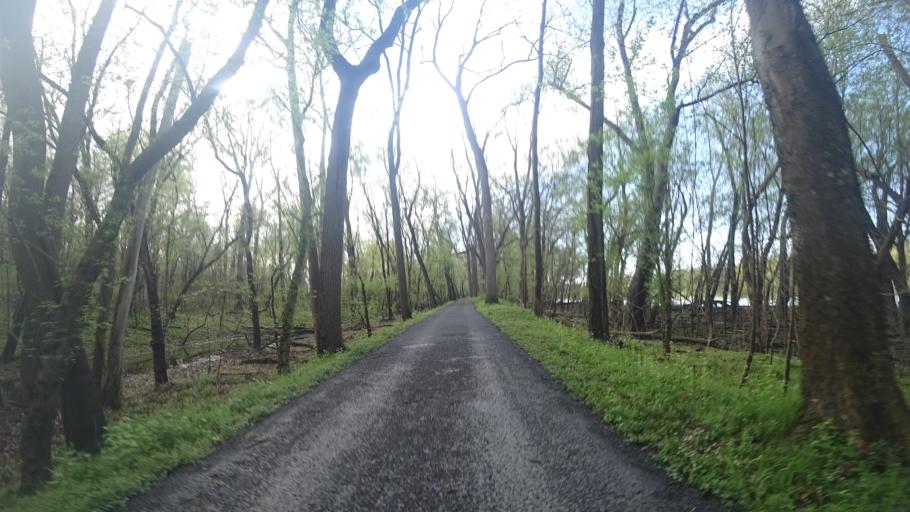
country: US
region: Virginia
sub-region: Loudoun County
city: University Center
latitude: 39.0950
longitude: -77.4682
